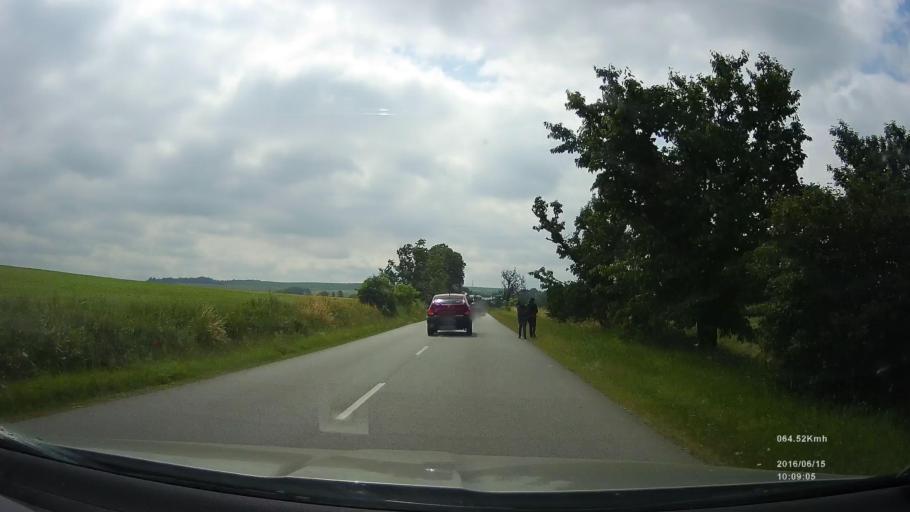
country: SK
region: Kosicky
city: Kosice
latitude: 48.7611
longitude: 21.3371
